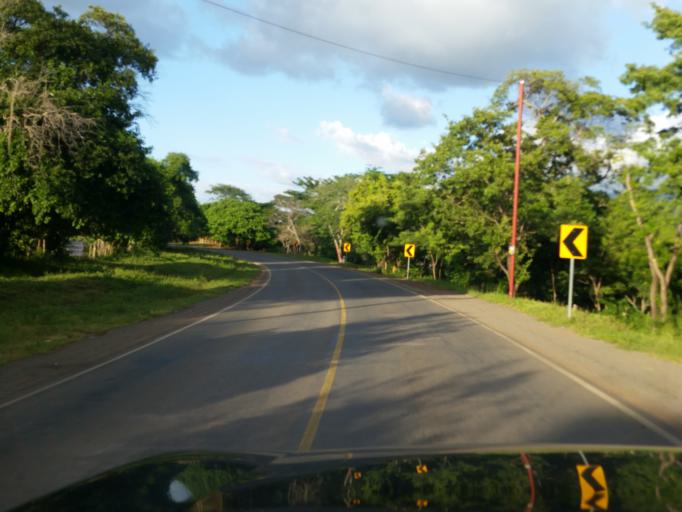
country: NI
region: Granada
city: Nandaime
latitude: 11.7788
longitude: -86.0506
